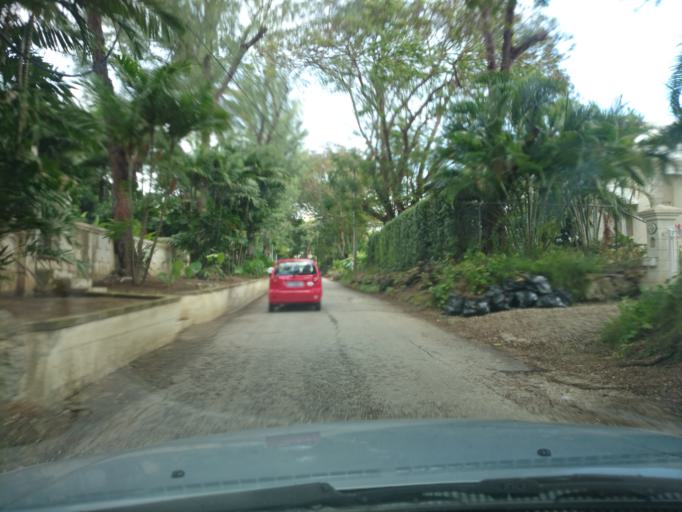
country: BB
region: Saint Peter
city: Speightstown
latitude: 13.2283
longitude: -59.6413
